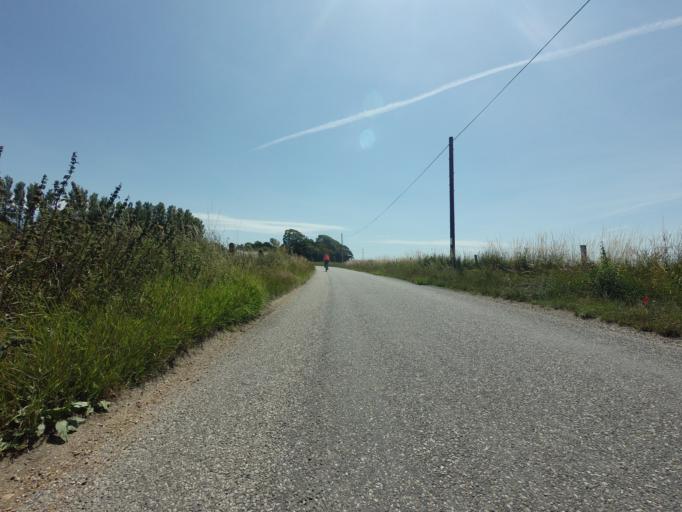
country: GB
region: England
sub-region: Kent
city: Lydd
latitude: 50.9605
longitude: 0.9029
